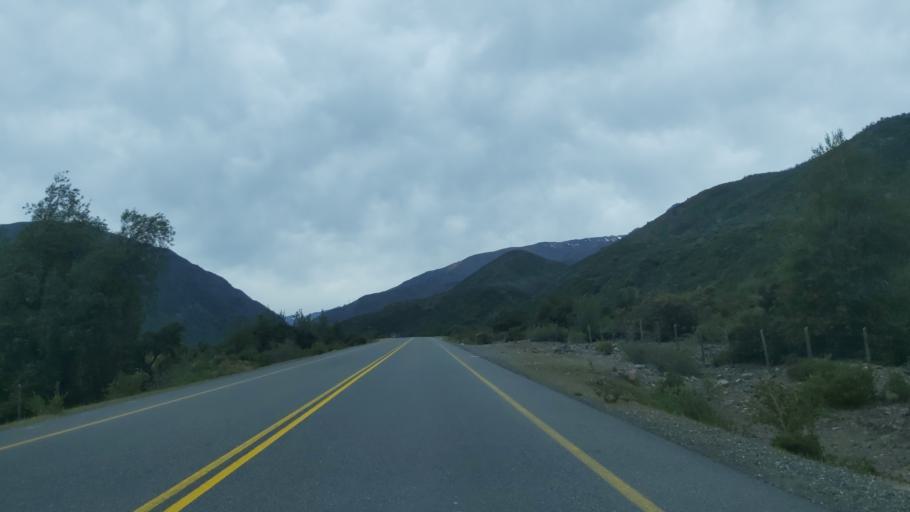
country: CL
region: Maule
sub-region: Provincia de Linares
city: Colbun
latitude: -35.8146
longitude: -70.8478
